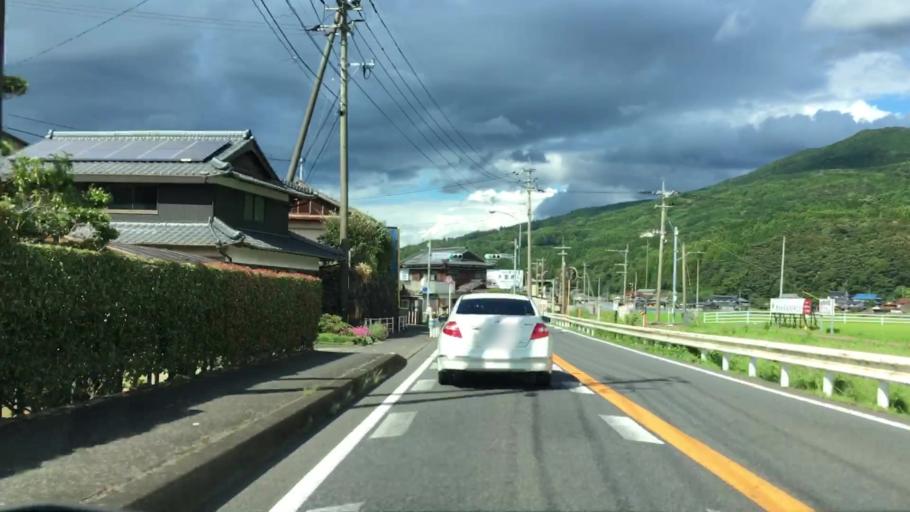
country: JP
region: Saga Prefecture
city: Imaricho-ko
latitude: 33.2283
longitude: 129.8485
